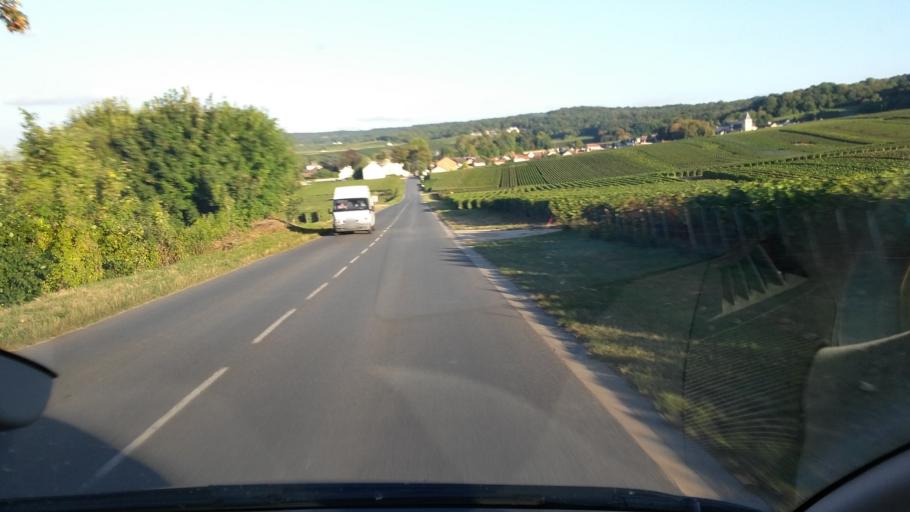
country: FR
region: Champagne-Ardenne
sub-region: Departement de la Marne
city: Rilly-la-Montagne
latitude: 49.1570
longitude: 4.0693
